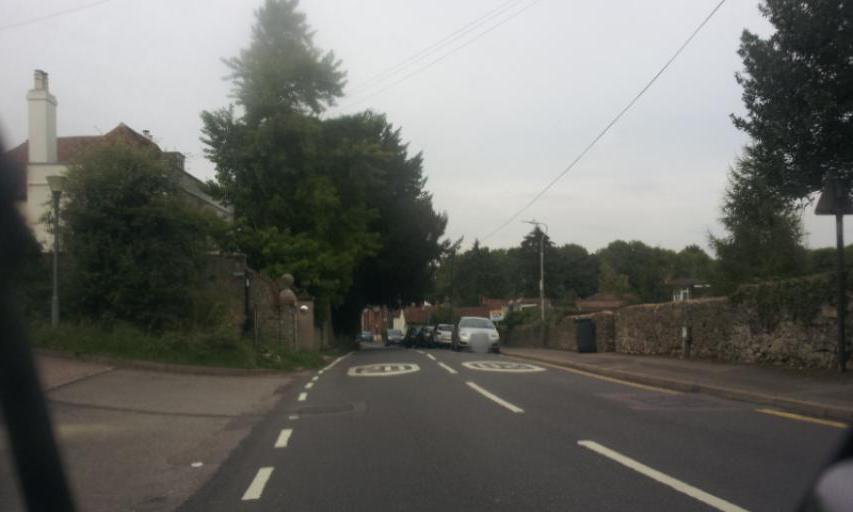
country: GB
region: England
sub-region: Kent
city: Larkfield
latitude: 51.2844
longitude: 0.4379
